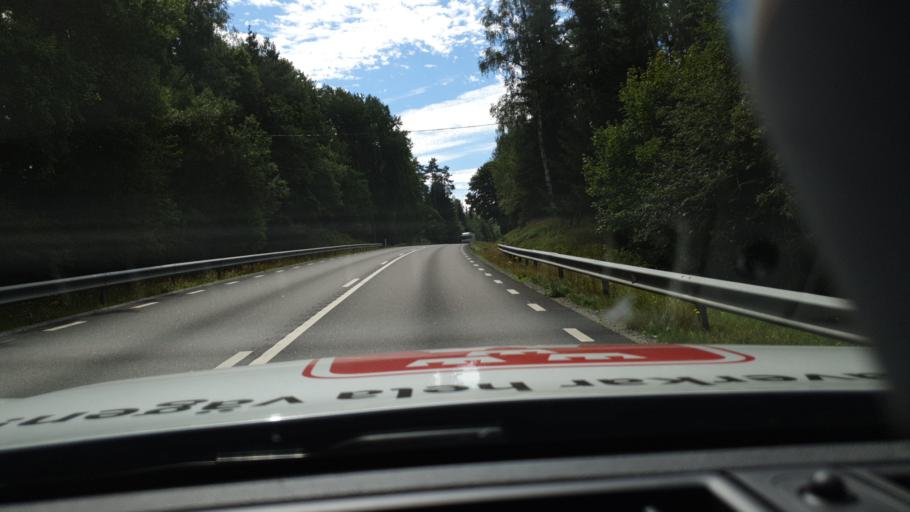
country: SE
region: Joenkoeping
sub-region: Savsjo Kommun
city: Stockaryd
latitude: 57.2735
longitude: 14.5236
